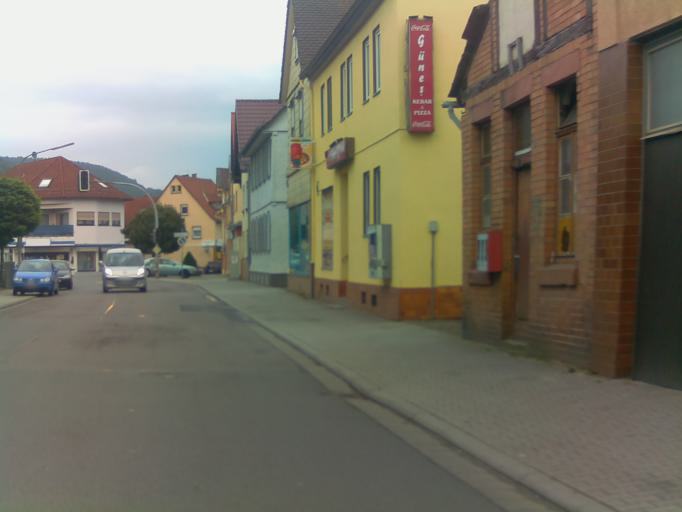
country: DE
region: Hesse
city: Hochst im Odenwald
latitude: 49.7967
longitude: 8.9933
